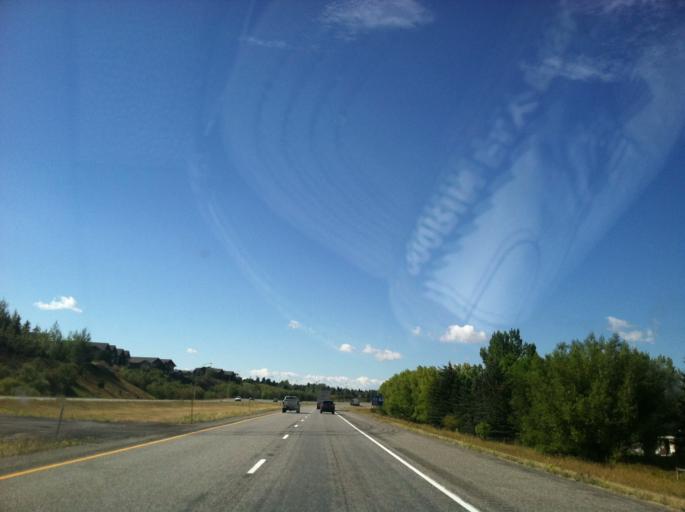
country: US
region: Montana
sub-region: Gallatin County
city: Bozeman
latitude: 45.6723
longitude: -111.0040
